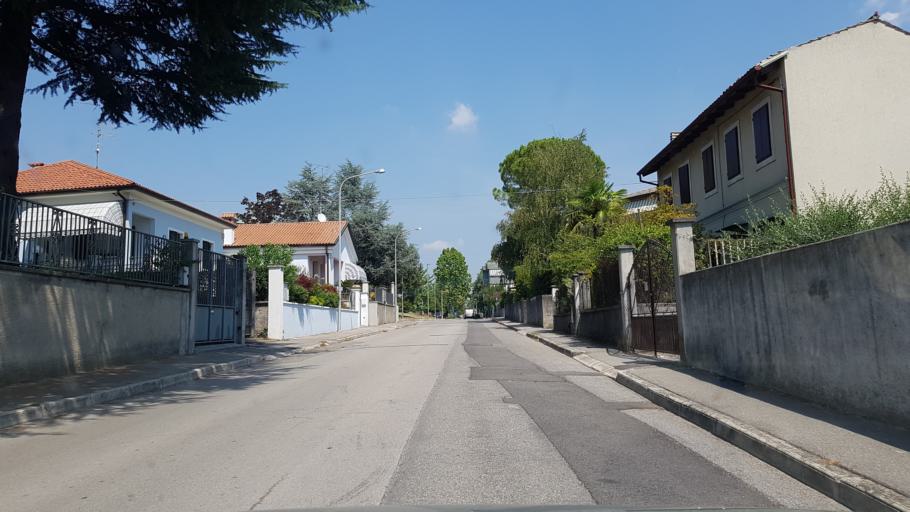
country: IT
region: Friuli Venezia Giulia
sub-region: Provincia di Gorizia
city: Gradisca d'Isonzo
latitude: 45.8891
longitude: 13.4939
